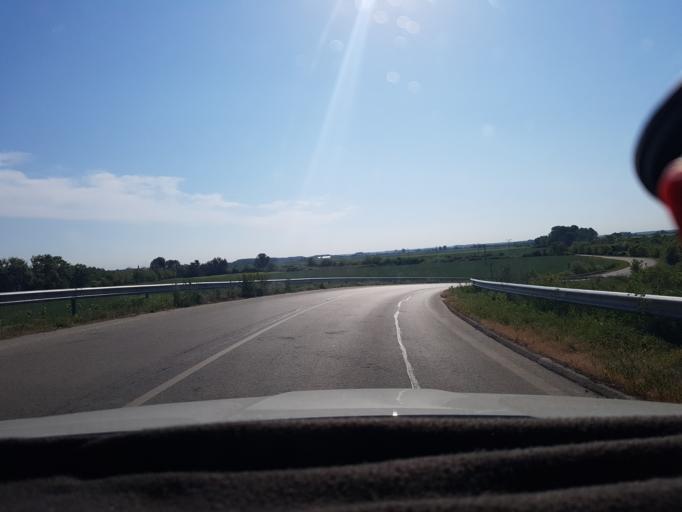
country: HU
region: Tolna
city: Decs
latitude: 46.2756
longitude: 18.7217
